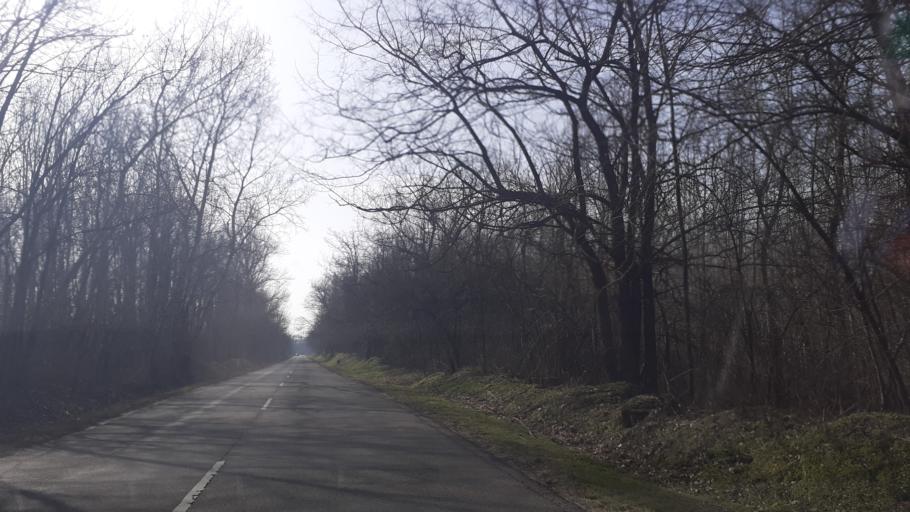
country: HU
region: Pest
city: Orkeny
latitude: 47.0951
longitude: 19.3847
